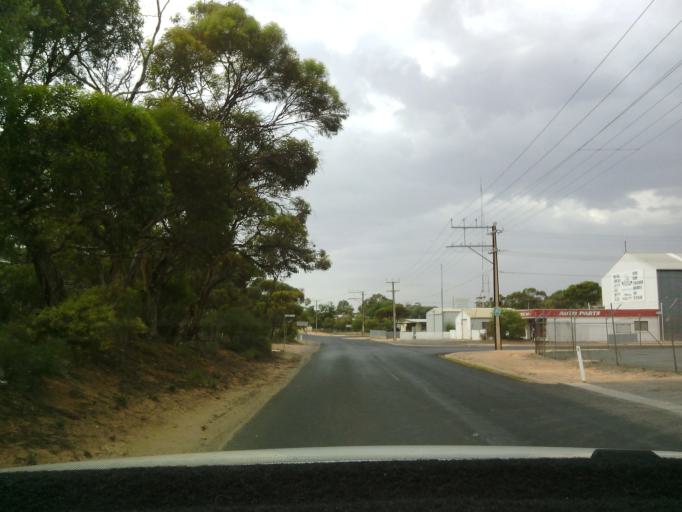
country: AU
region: South Australia
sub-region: Berri and Barmera
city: Berri
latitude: -34.2699
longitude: 140.6043
